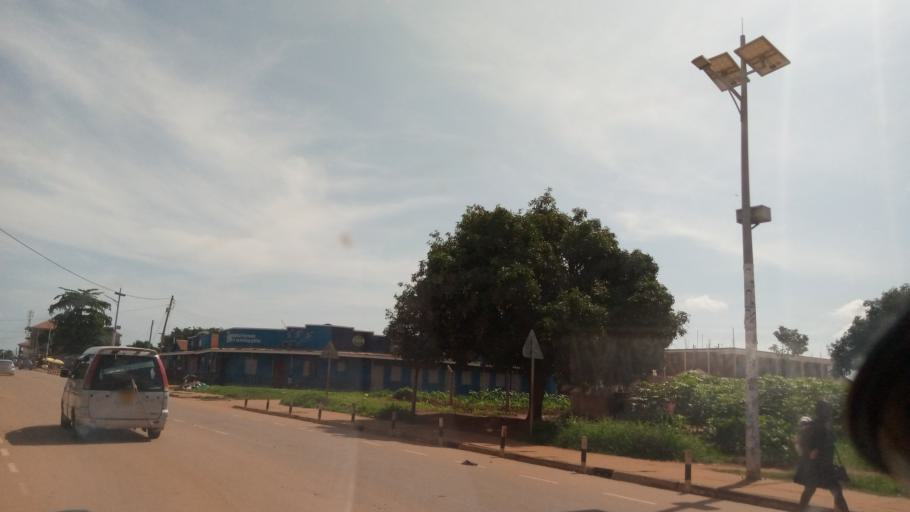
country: UG
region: Northern Region
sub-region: Gulu District
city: Gulu
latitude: 2.7652
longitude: 32.3057
